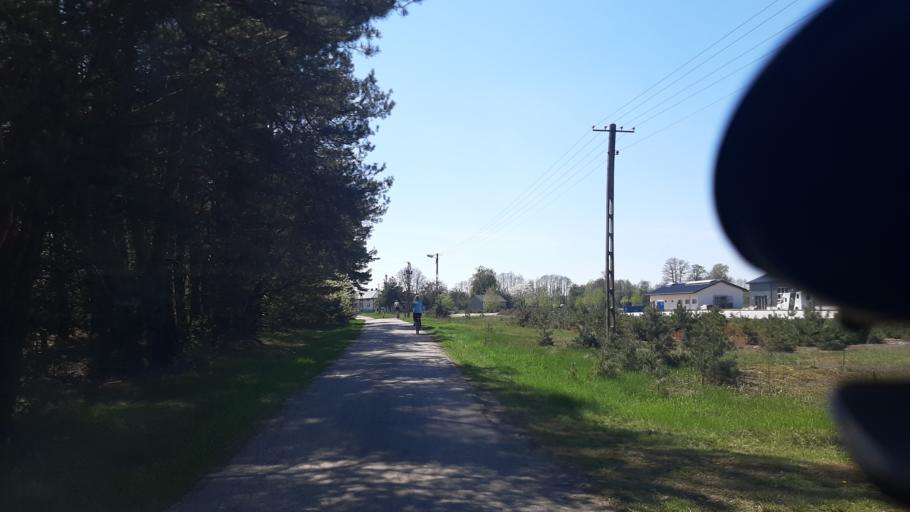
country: PL
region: Lublin Voivodeship
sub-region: Powiat lubartowski
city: Abramow
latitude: 51.4267
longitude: 22.2762
